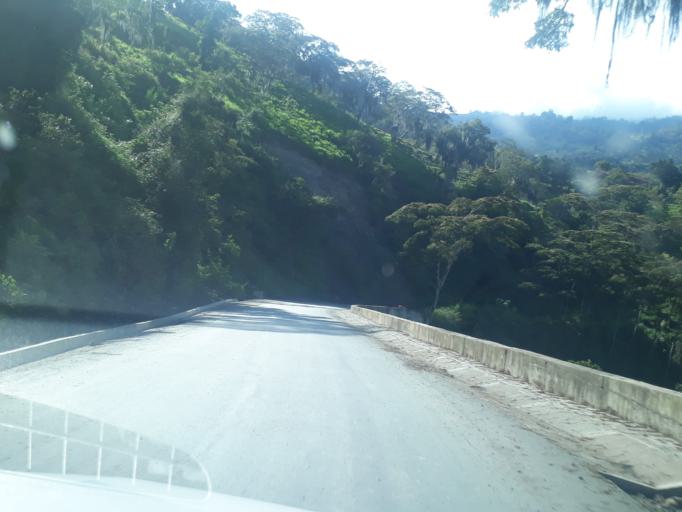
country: CO
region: Santander
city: Velez
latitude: 6.0401
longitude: -73.6526
